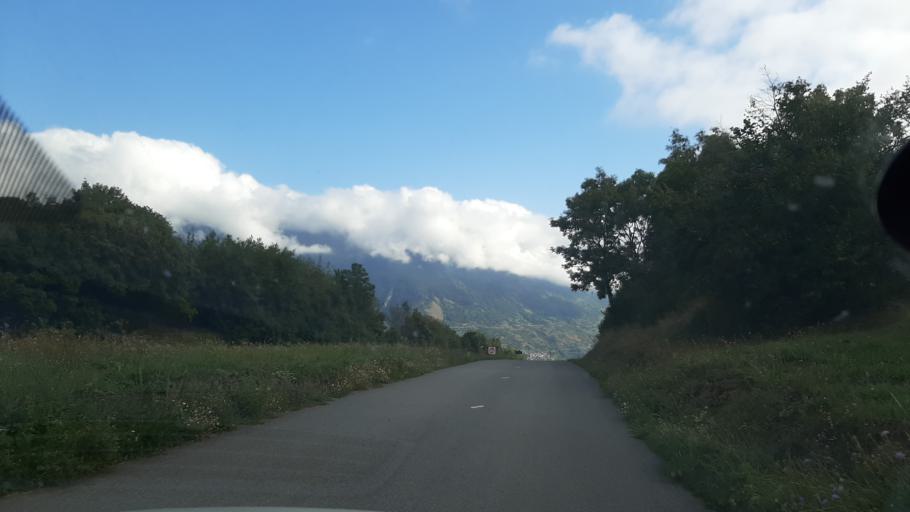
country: FR
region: Rhone-Alpes
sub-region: Departement de la Savoie
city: Aime
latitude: 45.5154
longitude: 6.5960
